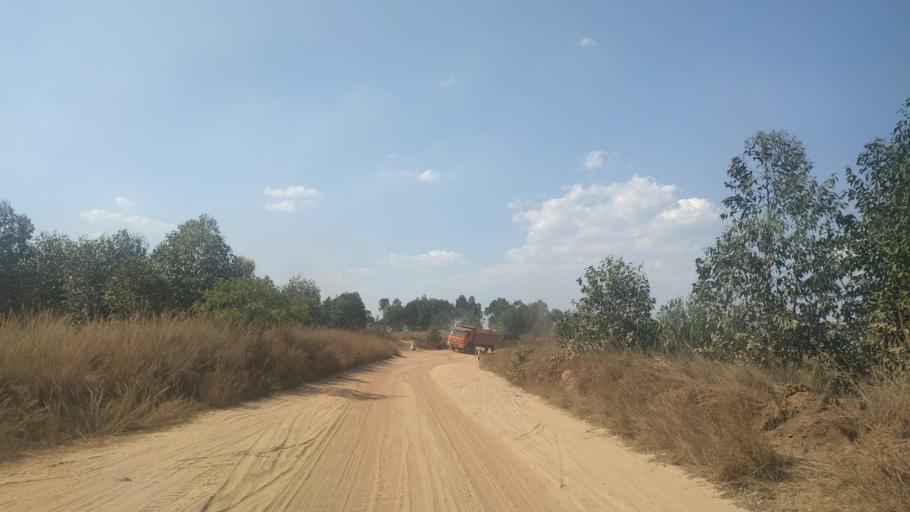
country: MG
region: Alaotra Mangoro
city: Ambatondrazaka
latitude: -18.0251
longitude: 48.2537
